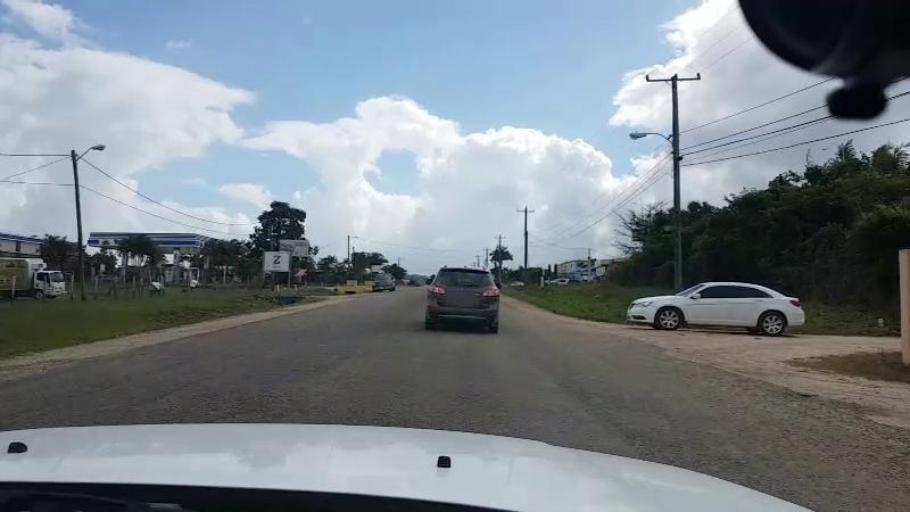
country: BZ
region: Cayo
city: Belmopan
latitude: 17.2460
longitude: -88.7836
